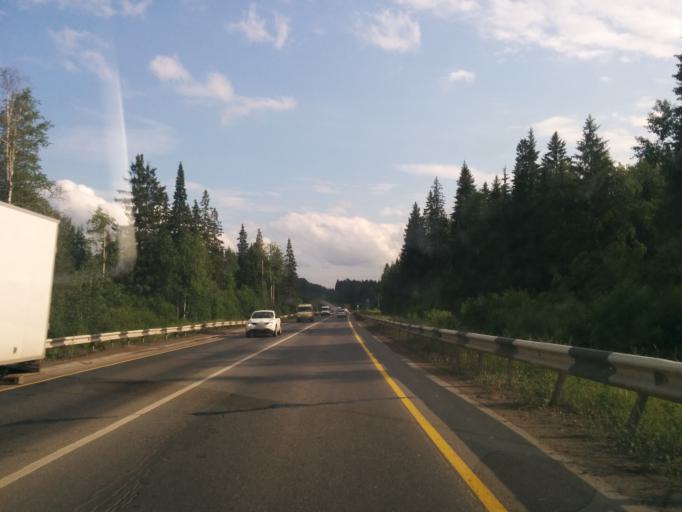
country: RU
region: Perm
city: Novyye Lyady
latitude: 58.0913
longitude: 56.4277
